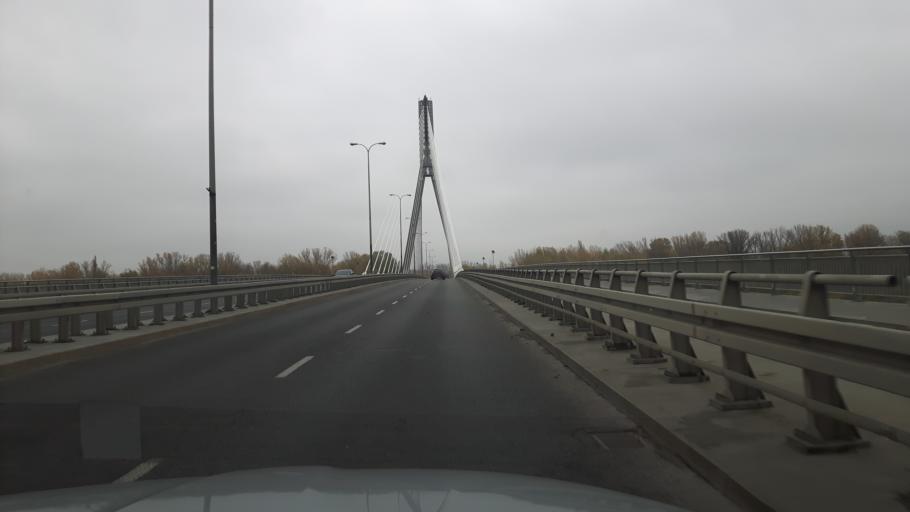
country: PL
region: Masovian Voivodeship
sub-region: Warszawa
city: Praga Polnoc
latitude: 52.2406
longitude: 21.0319
